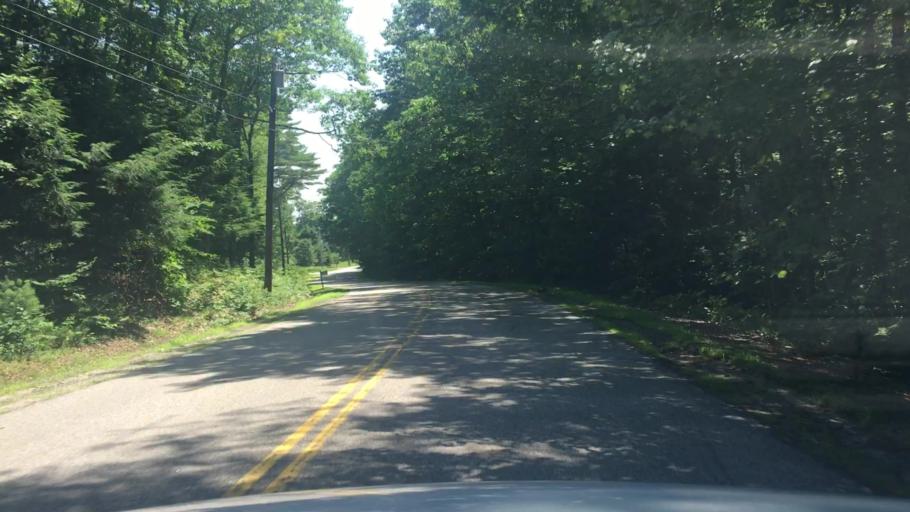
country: US
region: Maine
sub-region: Cumberland County
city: Cumberland Center
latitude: 43.7617
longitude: -70.2760
